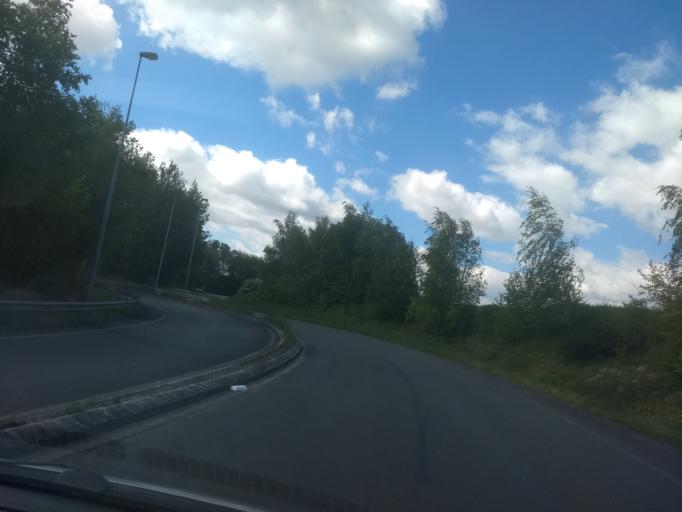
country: FR
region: Nord-Pas-de-Calais
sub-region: Departement du Pas-de-Calais
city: Saint-Laurent-Blangy
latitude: 50.3091
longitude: 2.8015
